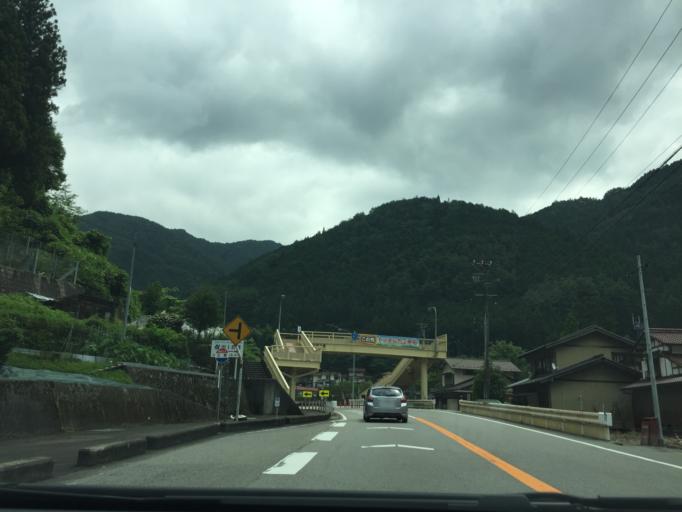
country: JP
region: Gifu
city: Gujo
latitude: 35.7795
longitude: 137.2519
